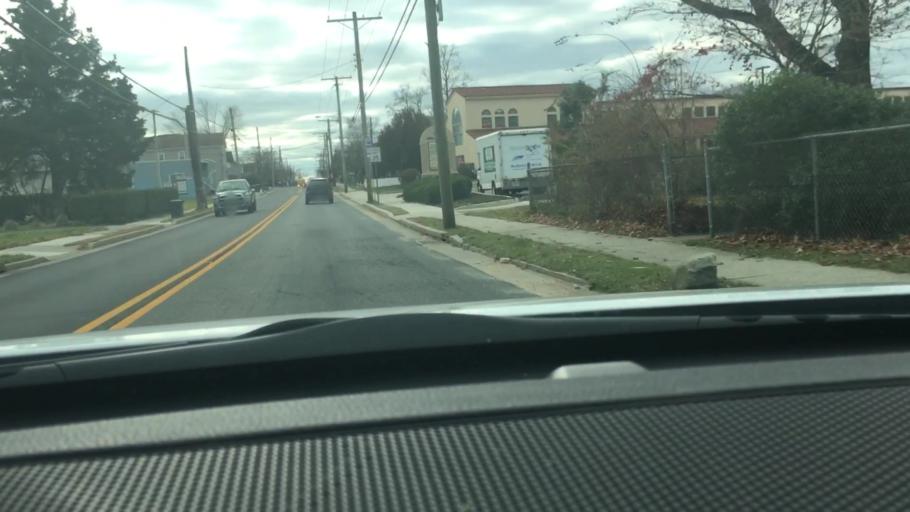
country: US
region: New Jersey
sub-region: Atlantic County
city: Pleasantville
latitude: 39.4012
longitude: -74.5141
